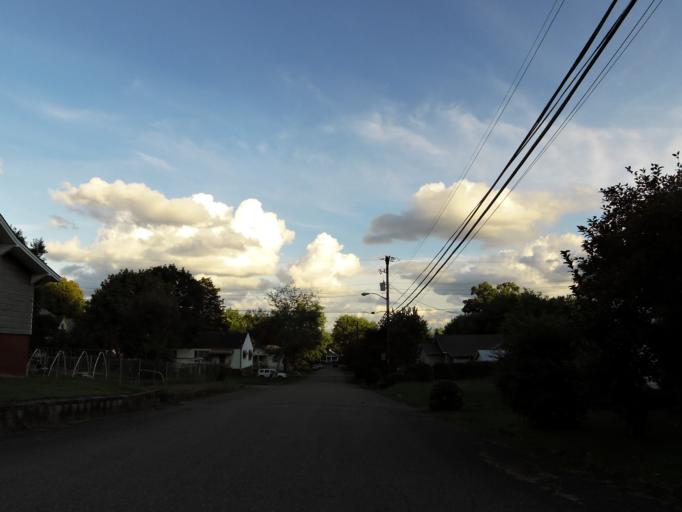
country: US
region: Tennessee
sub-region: Knox County
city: Knoxville
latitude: 36.0009
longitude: -83.9409
